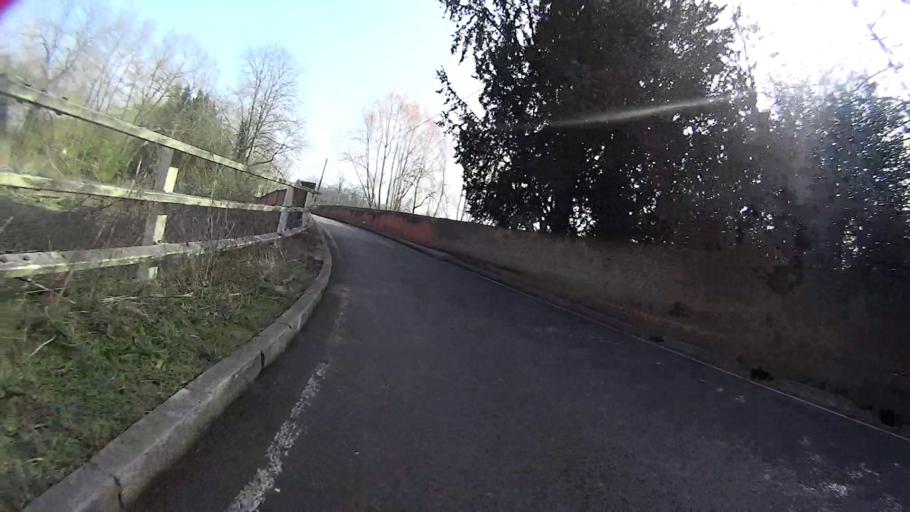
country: GB
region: England
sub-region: Surrey
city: Headley
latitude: 51.2319
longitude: -0.2659
